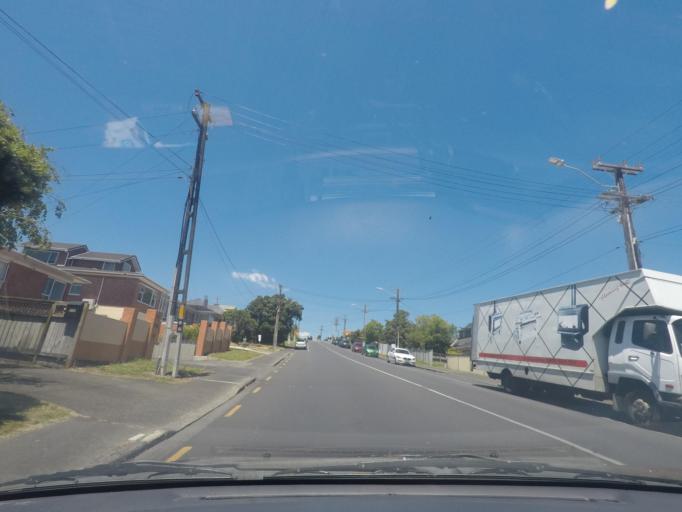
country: NZ
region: Auckland
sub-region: Auckland
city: Auckland
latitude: -36.9305
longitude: 174.7312
